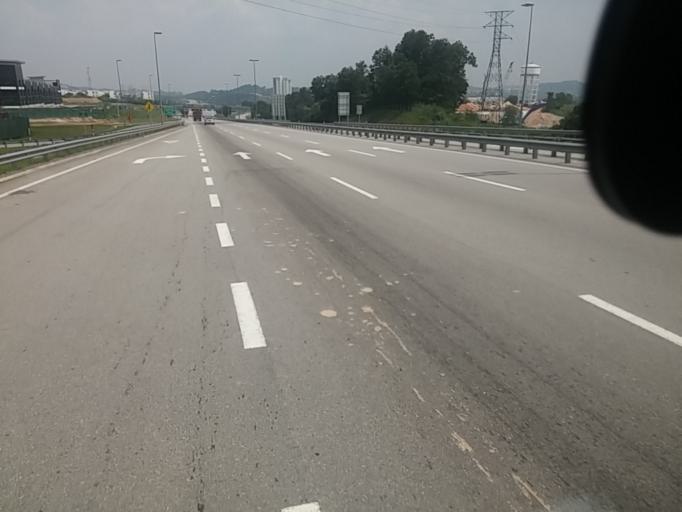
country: MY
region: Putrajaya
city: Putrajaya
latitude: 2.9743
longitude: 101.6609
